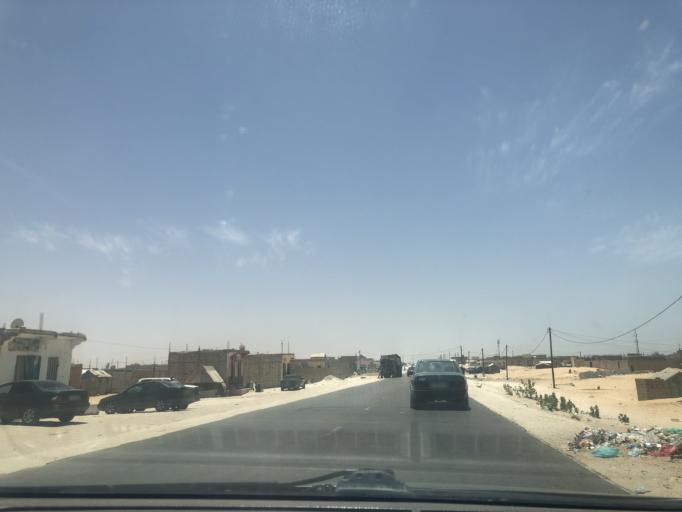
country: MR
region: Nouakchott
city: Nouakchott
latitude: 18.0104
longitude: -15.9594
